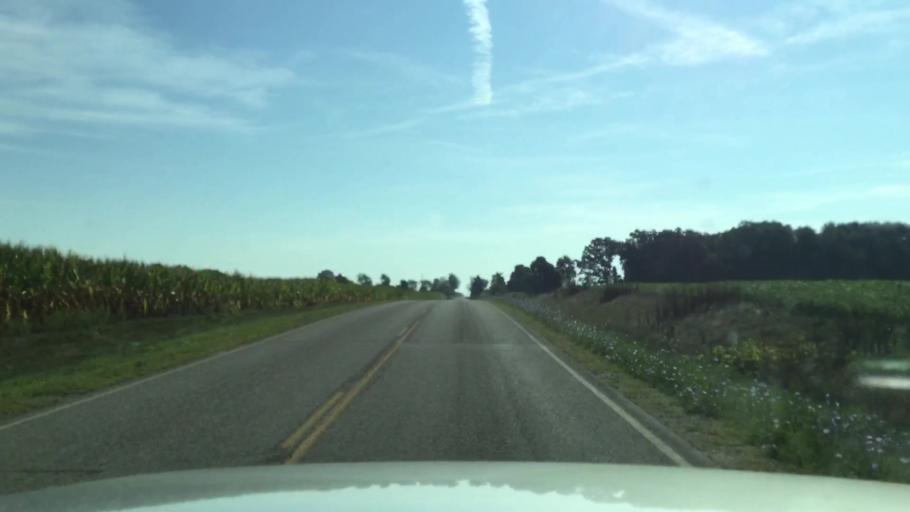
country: US
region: Michigan
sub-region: Lenawee County
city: Hudson
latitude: 41.9276
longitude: -84.3956
